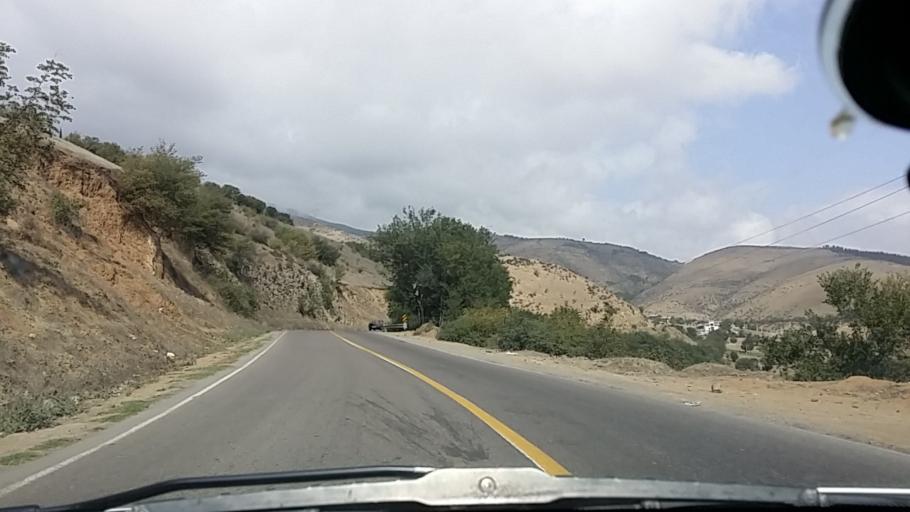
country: IR
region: Mazandaran
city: Chalus
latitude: 36.4626
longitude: 51.2793
